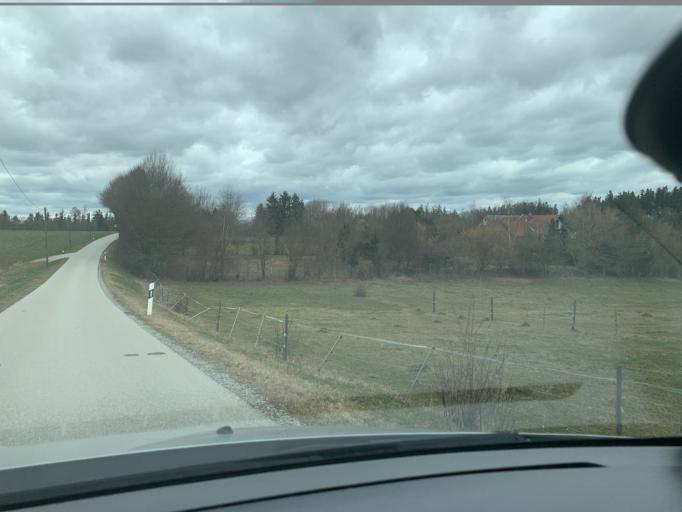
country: DE
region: Bavaria
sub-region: Lower Bavaria
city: Tiefenbach
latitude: 48.5015
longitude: 12.0869
